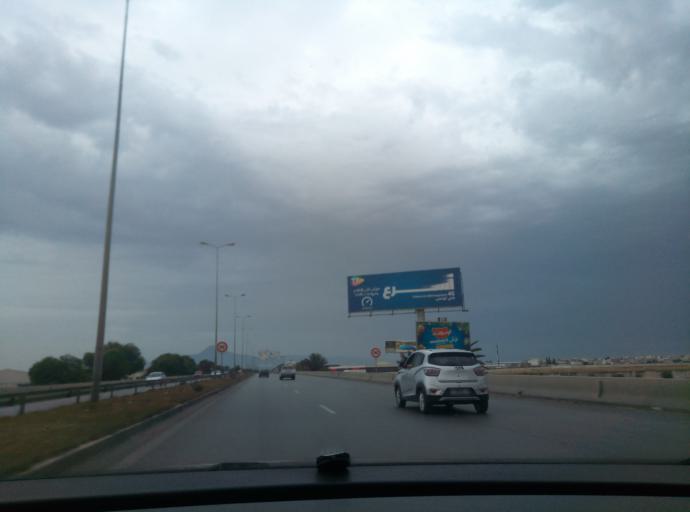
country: TN
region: Bin 'Arus
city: Ben Arous
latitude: 36.7322
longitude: 10.2291
